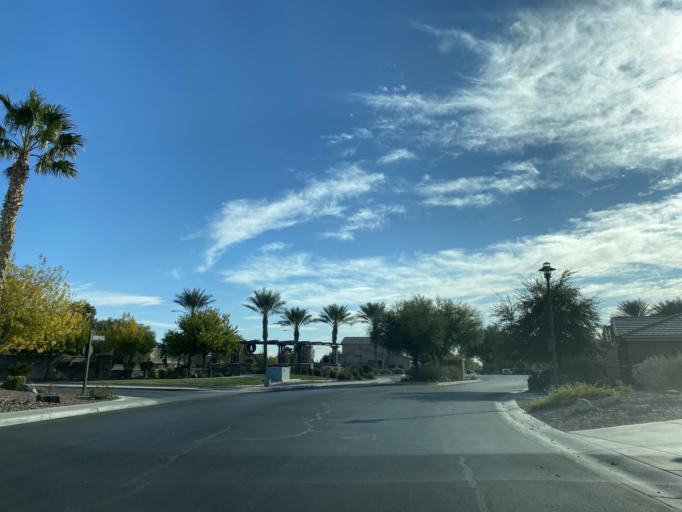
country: US
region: Nevada
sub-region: Clark County
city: North Las Vegas
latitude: 36.3134
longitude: -115.2429
